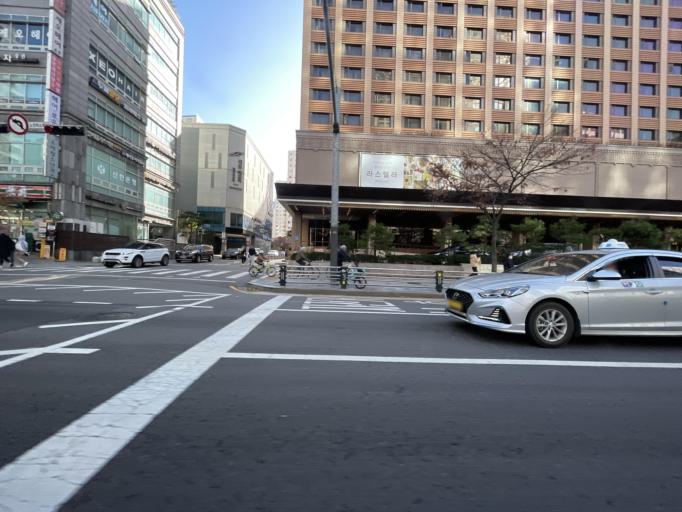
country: KR
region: Seoul
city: Seoul
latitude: 37.5411
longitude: 126.9483
